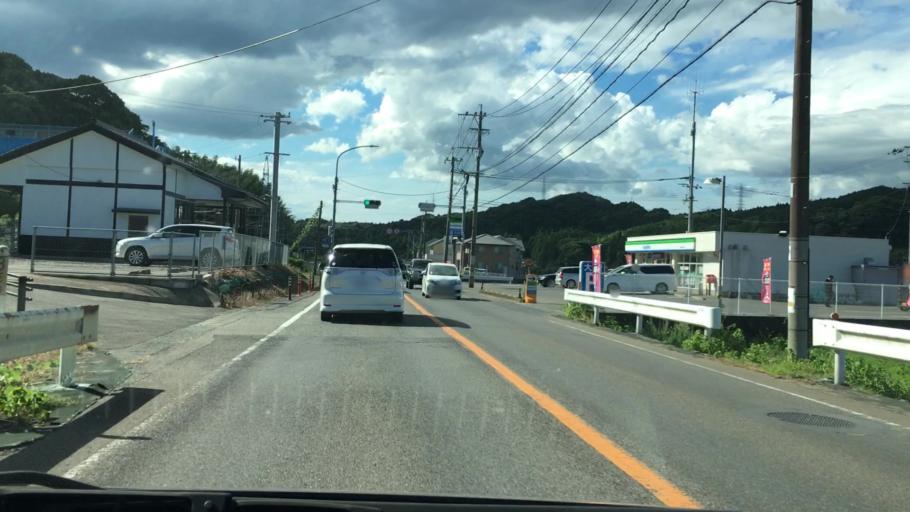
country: JP
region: Saga Prefecture
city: Takeocho-takeo
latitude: 33.1931
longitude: 129.9811
